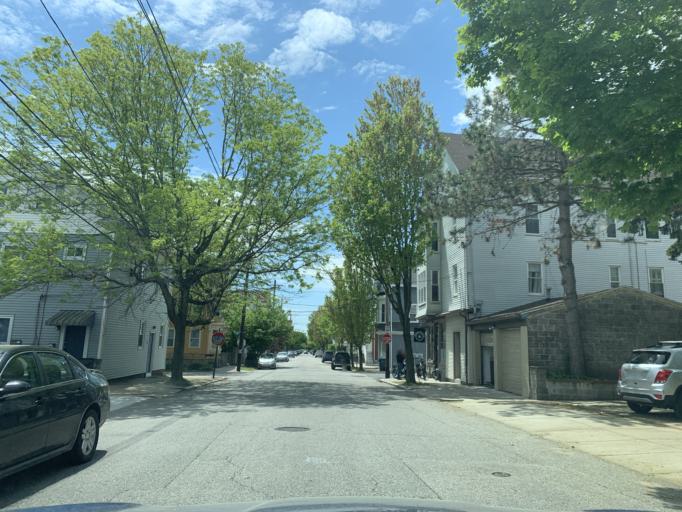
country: US
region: Rhode Island
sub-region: Providence County
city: Providence
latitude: 41.8241
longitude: -71.3924
